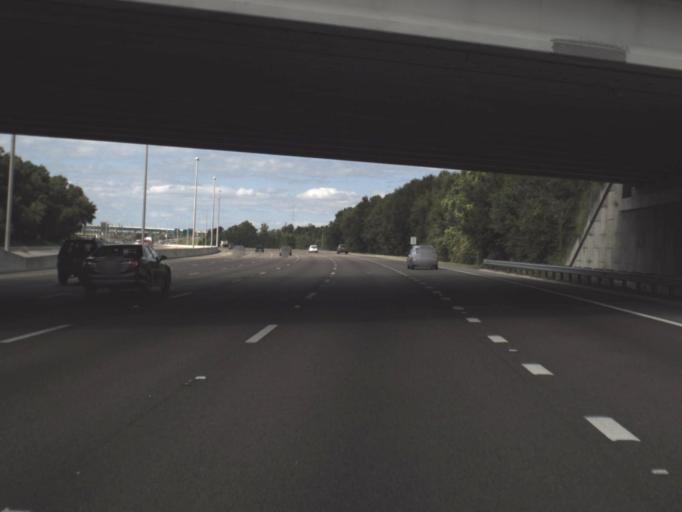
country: US
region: Florida
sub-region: Orange County
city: Ocoee
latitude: 28.5460
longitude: -81.5418
